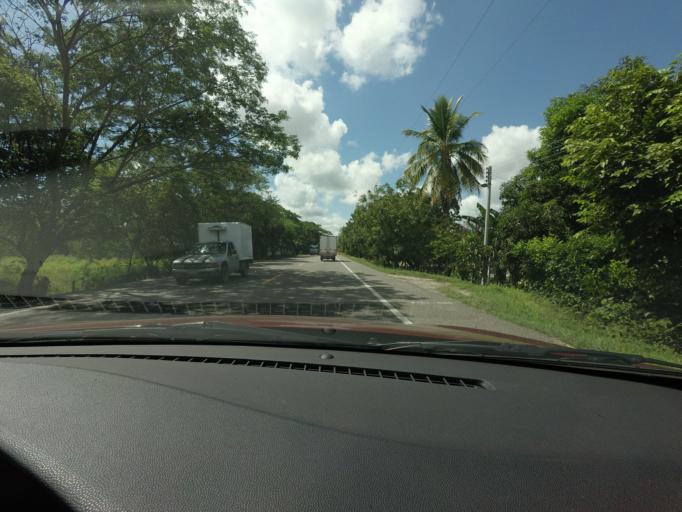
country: CO
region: Tolima
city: Saldana
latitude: 3.9444
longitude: -75.0110
